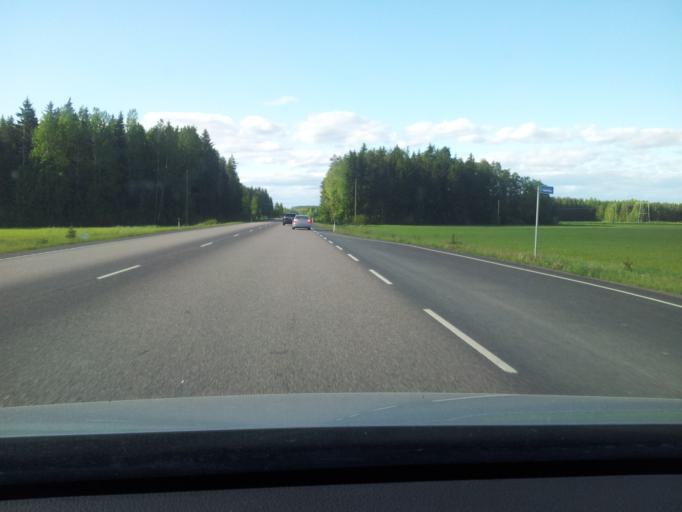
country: FI
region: Kymenlaakso
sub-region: Kouvola
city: Elimaeki
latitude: 60.8312
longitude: 26.5395
